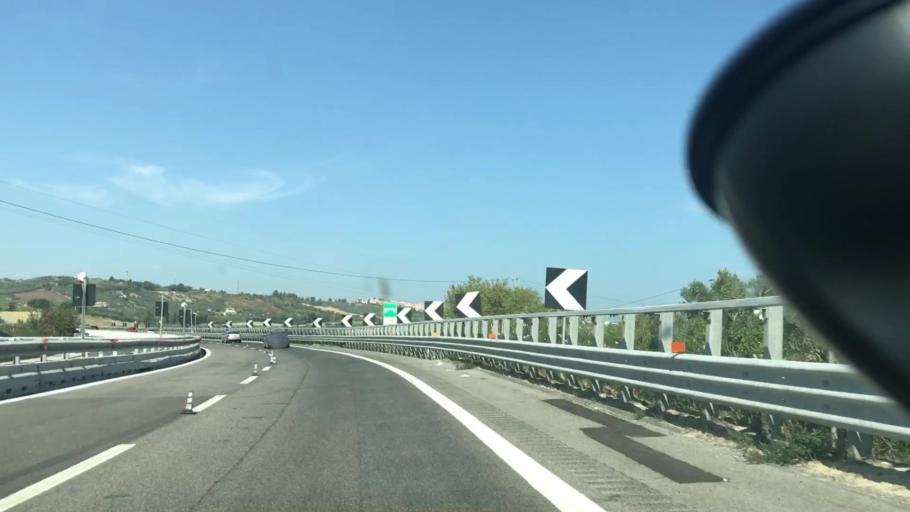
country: IT
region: Abruzzo
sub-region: Provincia di Chieti
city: Marina di Vasto
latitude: 42.0778
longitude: 14.7107
